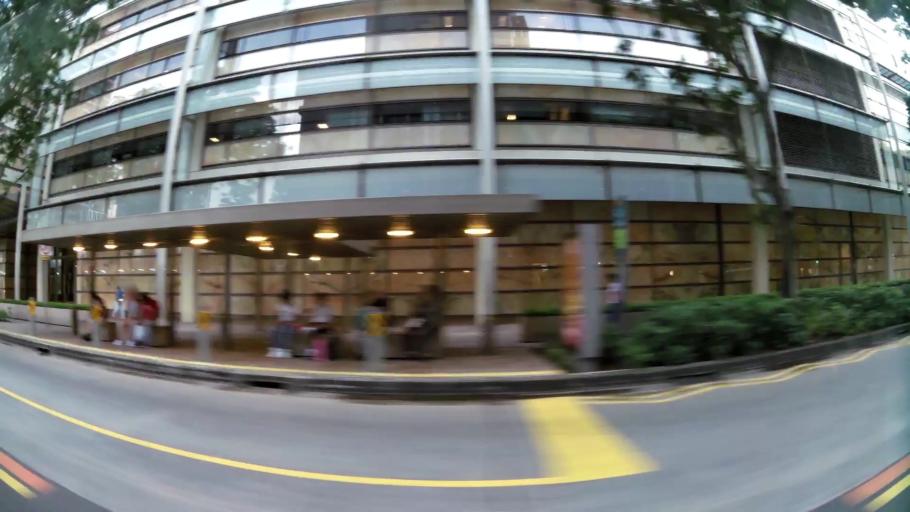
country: SG
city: Singapore
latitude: 1.2903
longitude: 103.8502
